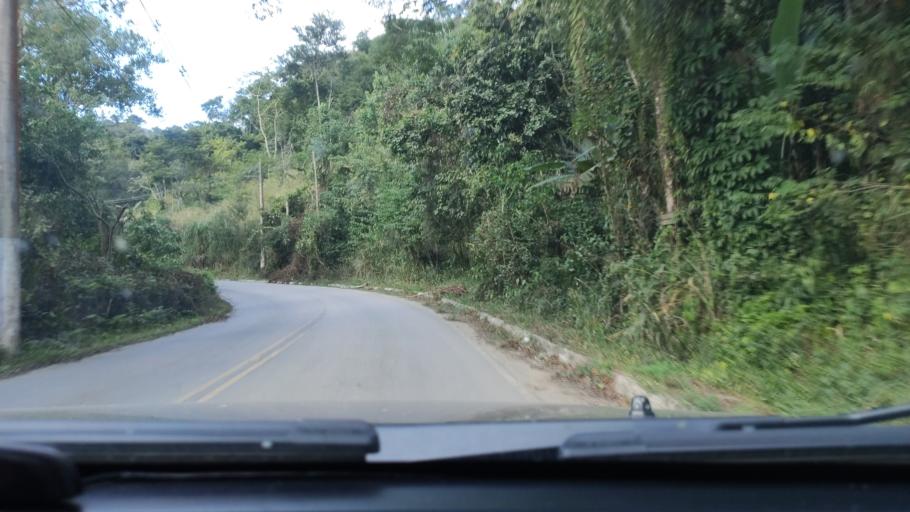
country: BR
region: Sao Paulo
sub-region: Sao Sebastiao
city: Sao Sebastiao
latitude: -23.7008
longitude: -45.4734
